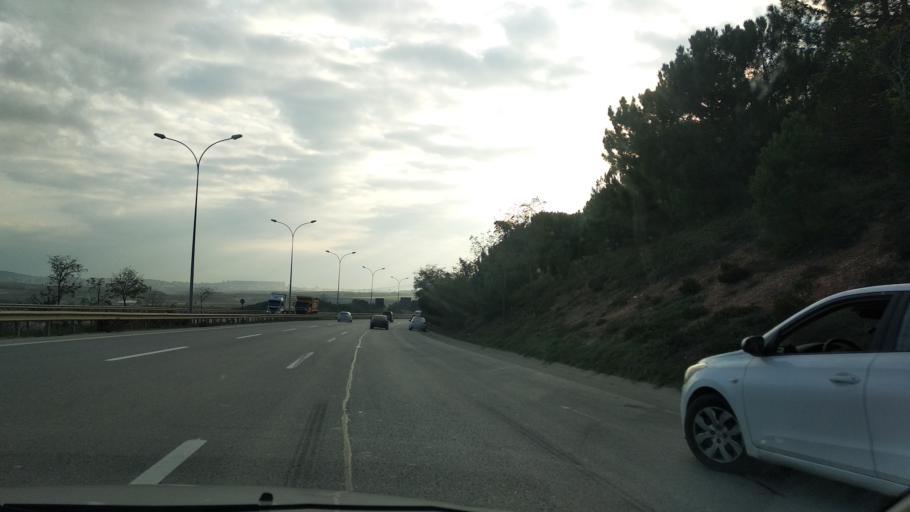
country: TR
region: Istanbul
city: Pendik
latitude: 40.9194
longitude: 29.3384
